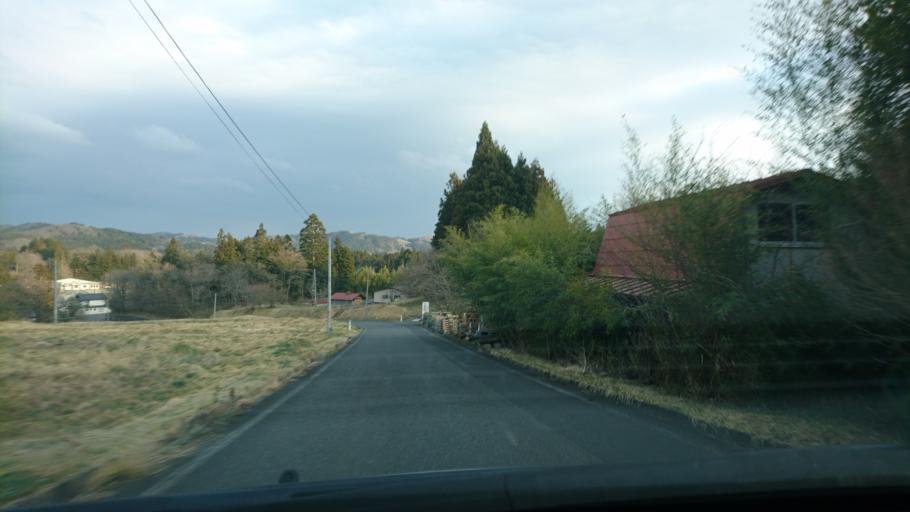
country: JP
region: Iwate
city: Ichinoseki
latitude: 38.8914
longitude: 141.2459
